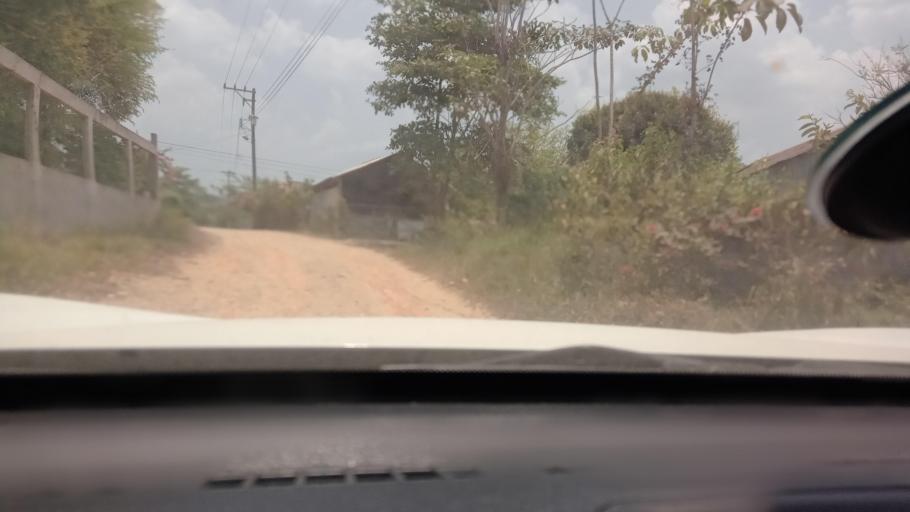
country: MX
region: Tabasco
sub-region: Huimanguillo
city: Francisco Rueda
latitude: 17.5231
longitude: -93.8840
